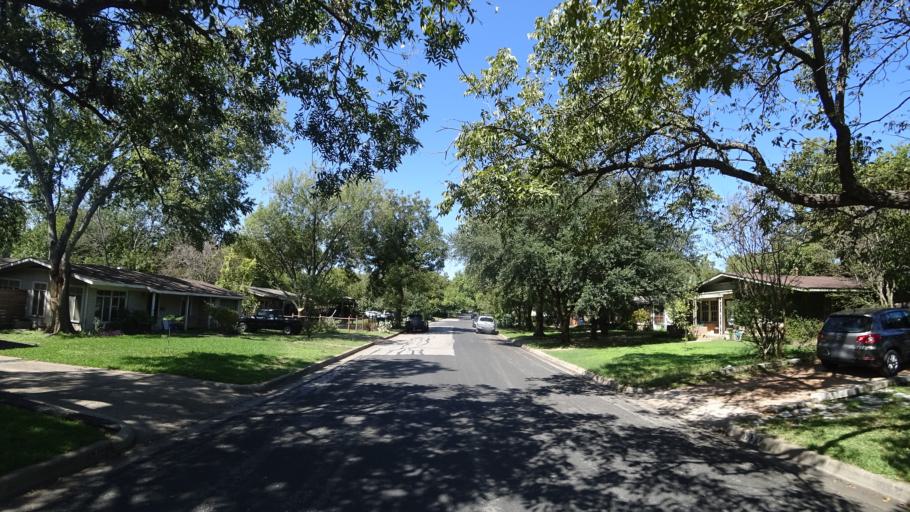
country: US
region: Texas
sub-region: Travis County
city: Austin
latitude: 30.3120
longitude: -97.7017
